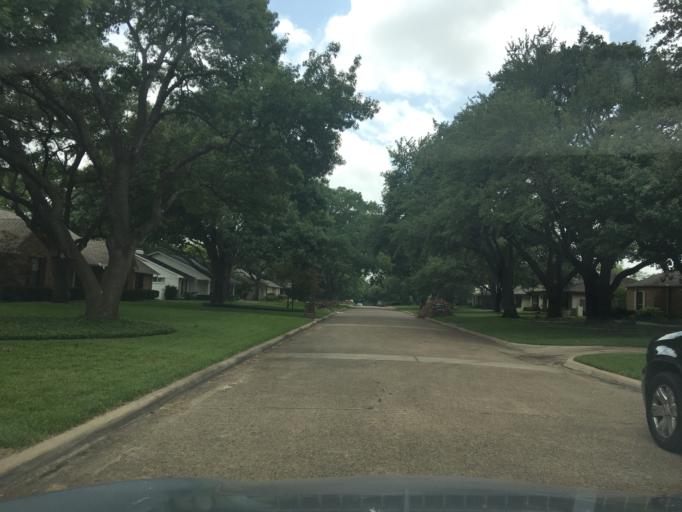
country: US
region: Texas
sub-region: Dallas County
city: Addison
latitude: 32.9081
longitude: -96.8311
